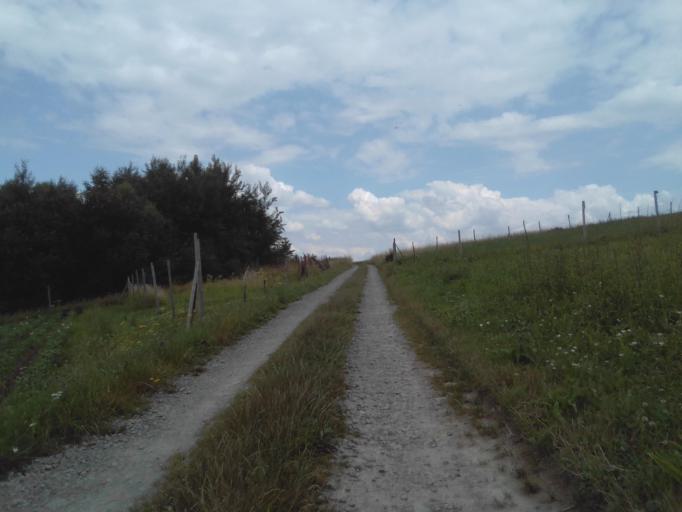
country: PL
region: Subcarpathian Voivodeship
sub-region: Powiat strzyzowski
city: Strzyzow
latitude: 49.8861
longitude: 21.7880
